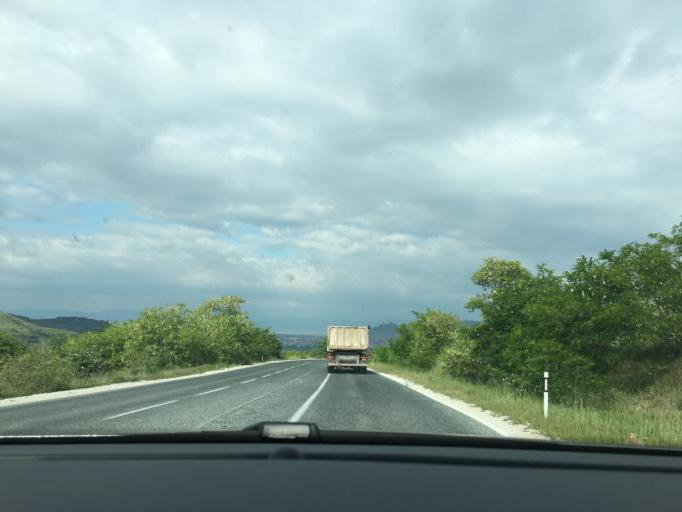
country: MK
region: Prilep
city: Prilep
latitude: 41.3694
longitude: 21.6321
